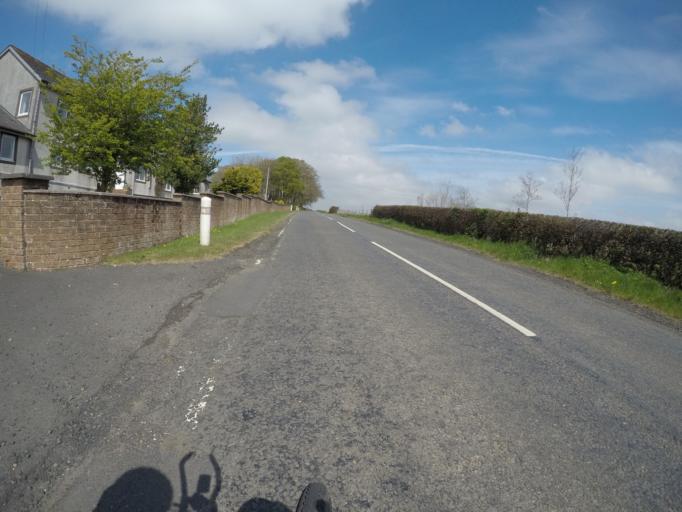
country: GB
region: Scotland
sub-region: East Ayrshire
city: Stewarton
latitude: 55.6984
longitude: -4.4856
